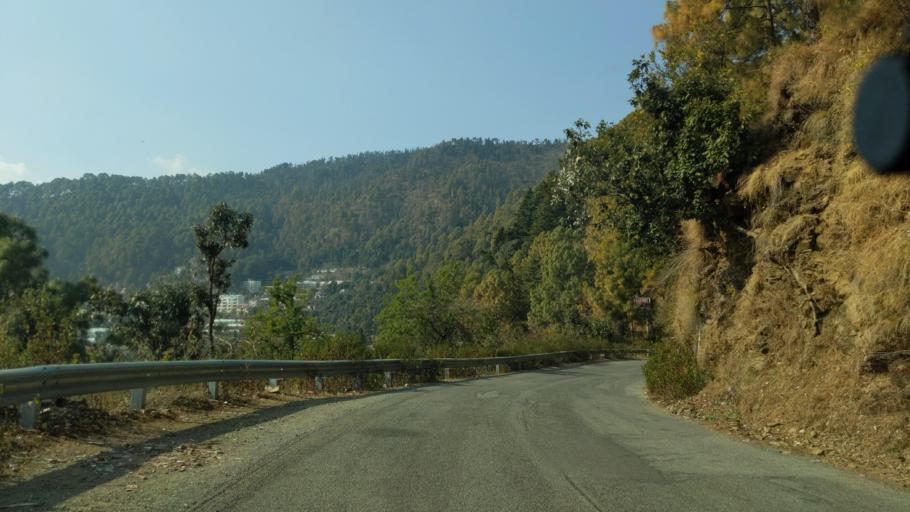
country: IN
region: Uttarakhand
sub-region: Naini Tal
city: Bhowali
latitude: 29.3901
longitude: 79.5365
